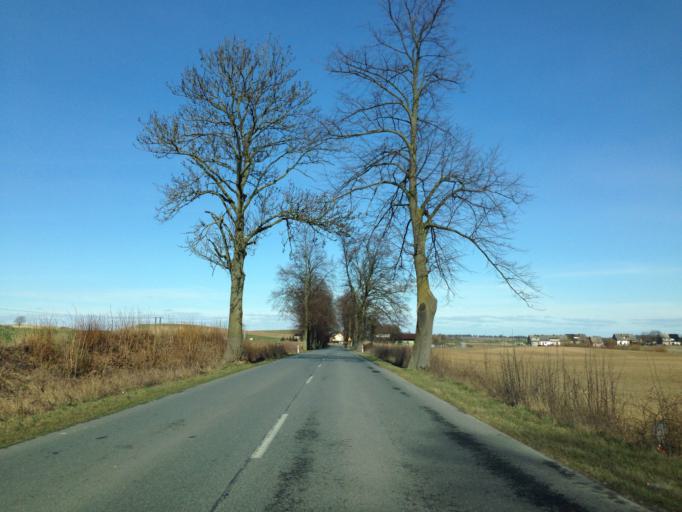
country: PL
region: Pomeranian Voivodeship
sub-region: Powiat sztumski
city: Stary Targ
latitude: 53.9899
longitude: 19.1083
